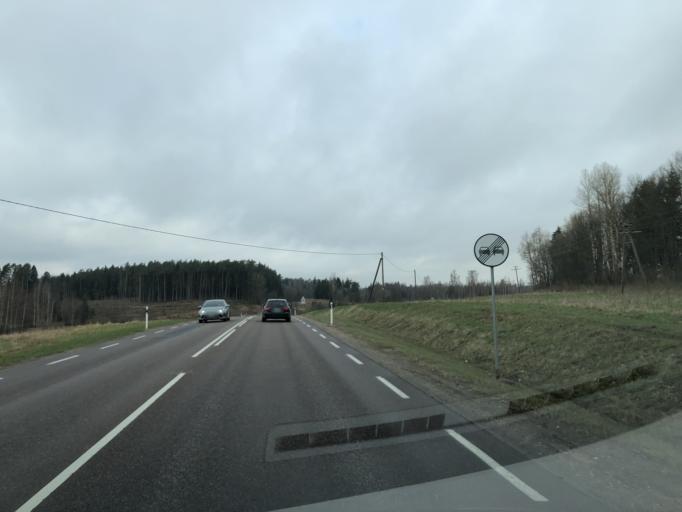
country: EE
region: Jogevamaa
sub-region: Jogeva linn
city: Jogeva
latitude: 58.6915
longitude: 26.4555
